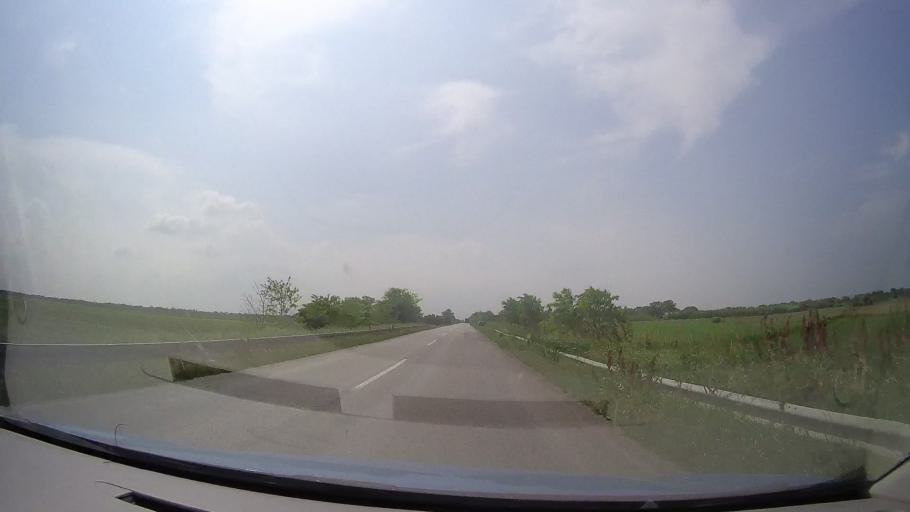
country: RS
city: Crepaja
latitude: 44.9517
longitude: 20.6630
